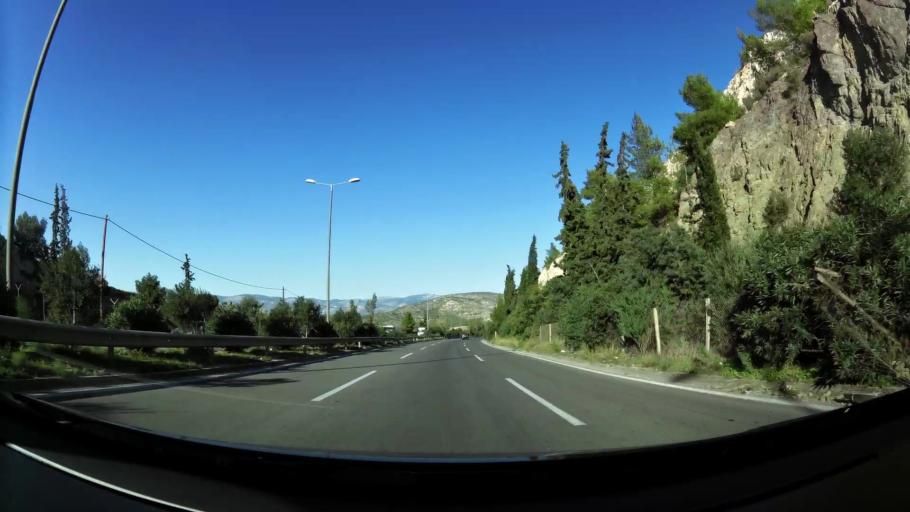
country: GR
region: Attica
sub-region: Nomarchia Athinas
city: Skaramangas
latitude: 37.9967
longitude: 23.5973
